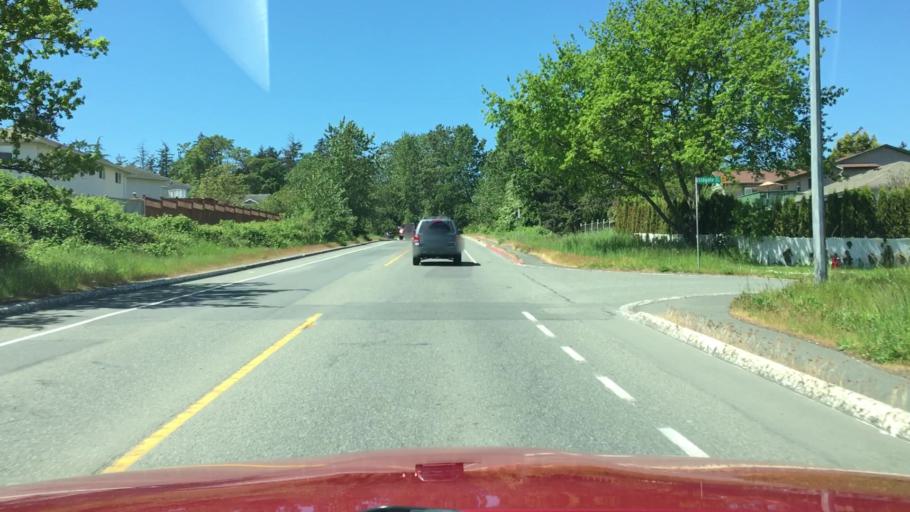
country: CA
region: British Columbia
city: Victoria
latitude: 48.4743
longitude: -123.4148
